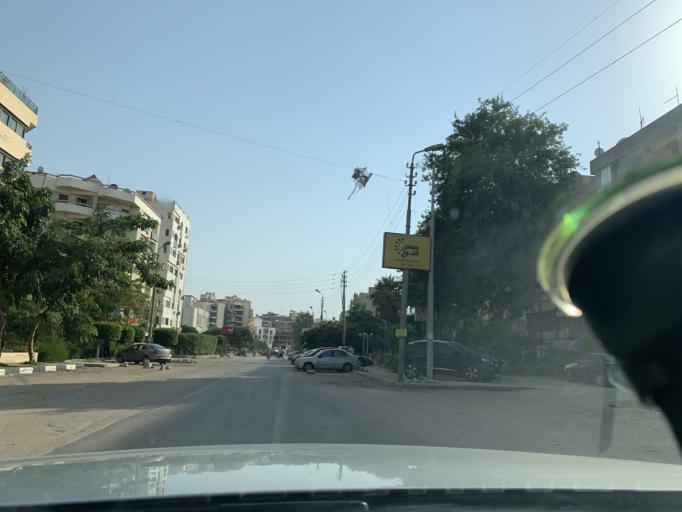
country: EG
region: Muhafazat al Qalyubiyah
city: Al Khankah
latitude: 30.1014
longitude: 31.3769
